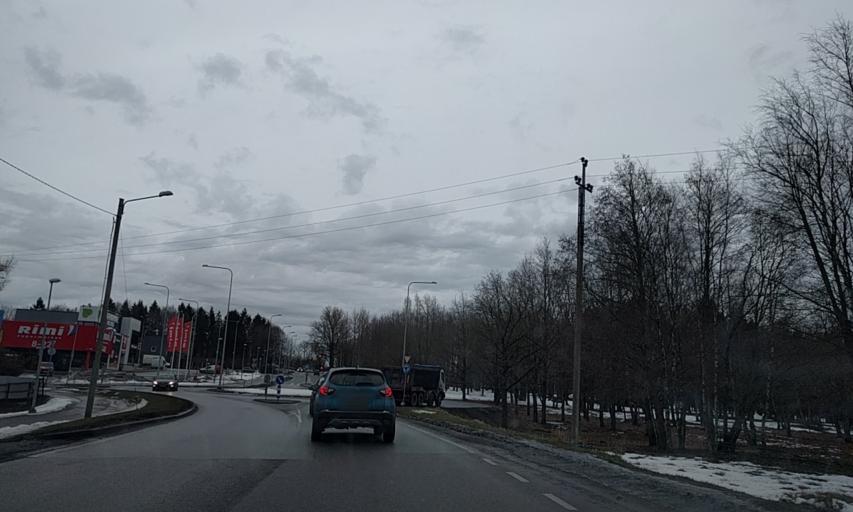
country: EE
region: Harju
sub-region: Tallinna linn
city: Kose
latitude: 59.4629
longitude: 24.9037
